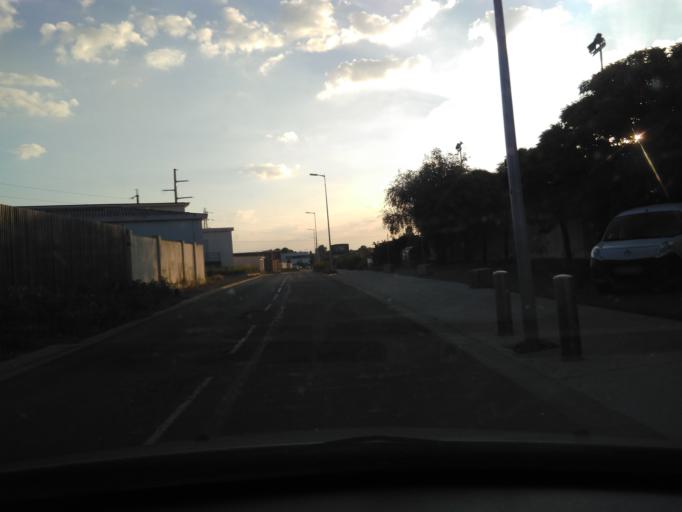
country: FR
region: Poitou-Charentes
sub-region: Departement de la Charente-Maritime
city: Puilboreau
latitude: 46.1752
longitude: -1.1194
